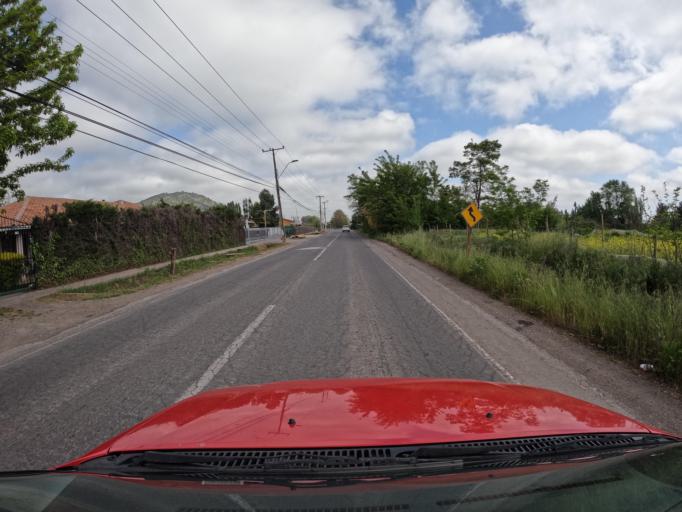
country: CL
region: O'Higgins
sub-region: Provincia de Colchagua
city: Santa Cruz
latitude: -34.7101
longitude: -71.2928
